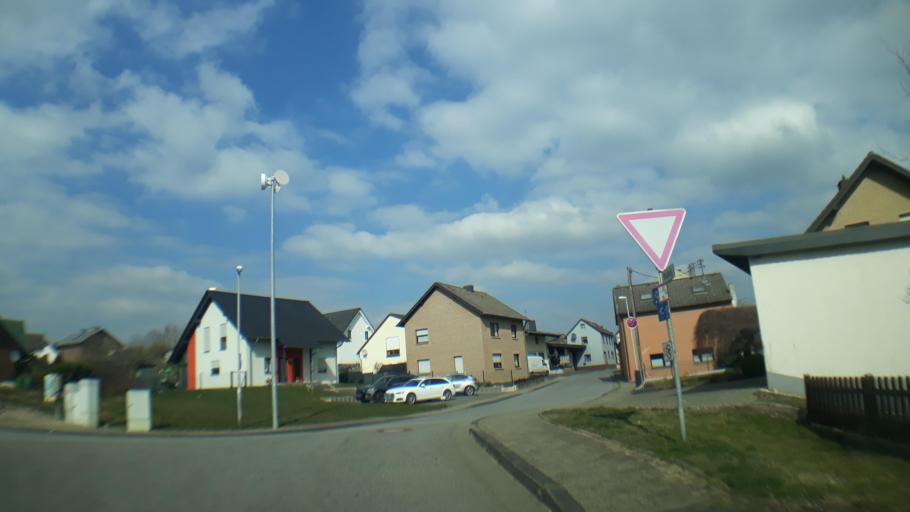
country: DE
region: Rheinland-Pfalz
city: Berg
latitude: 50.5530
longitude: 6.9461
